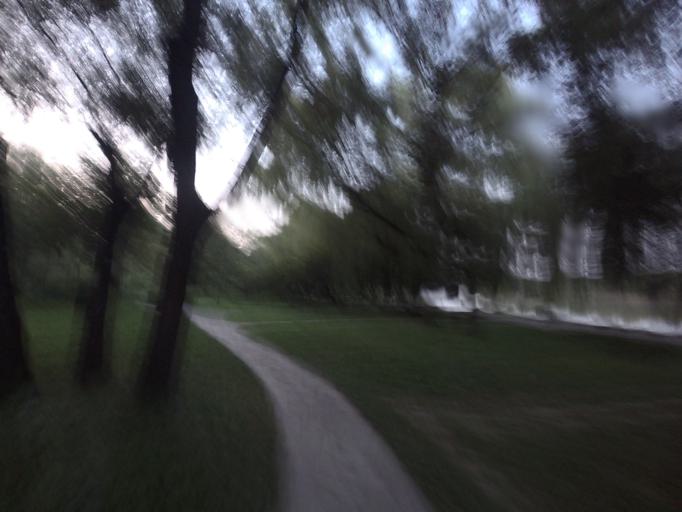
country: CN
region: Beijing
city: Haidian
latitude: 39.9806
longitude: 116.2711
